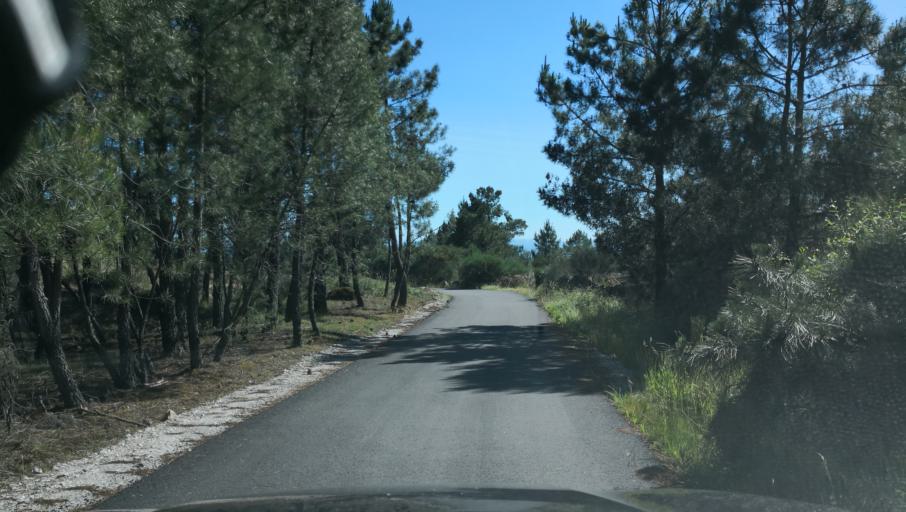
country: PT
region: Vila Real
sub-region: Vila Real
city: Vila Real
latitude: 41.3046
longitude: -7.6704
